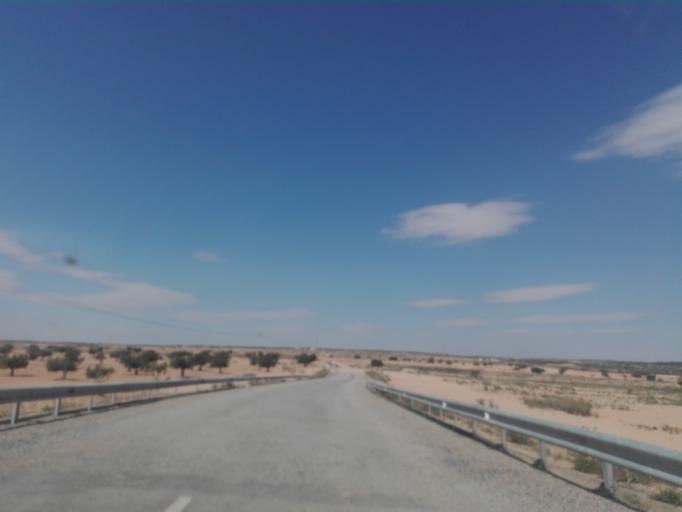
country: TN
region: Safaqis
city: Sfax
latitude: 34.6867
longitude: 10.5525
